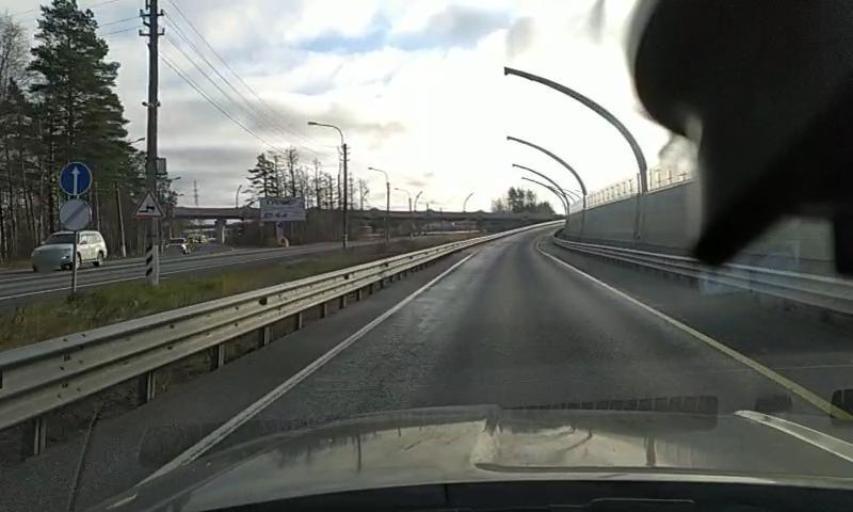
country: RU
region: St.-Petersburg
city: Solnechnoye
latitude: 60.1523
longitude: 29.9696
